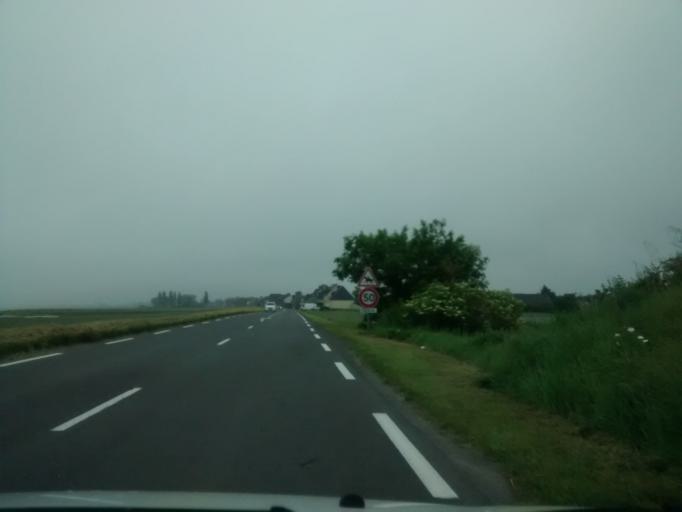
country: FR
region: Brittany
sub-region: Departement d'Ille-et-Vilaine
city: La Fresnais
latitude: 48.6261
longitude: -1.8591
